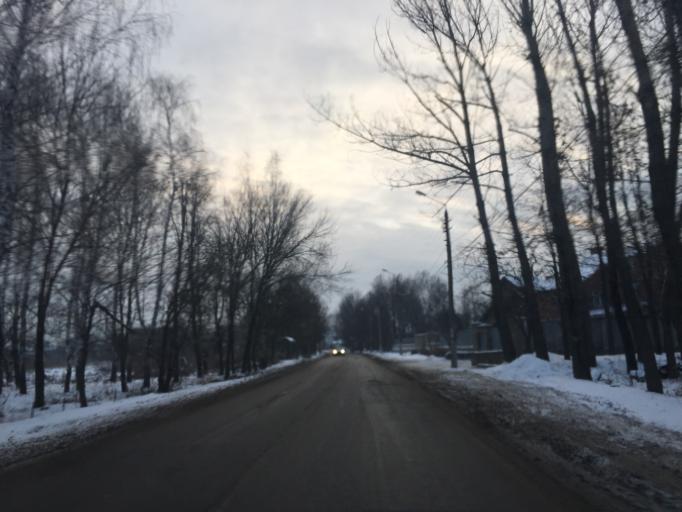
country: RU
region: Tula
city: Gorelki
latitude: 54.2354
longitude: 37.6425
